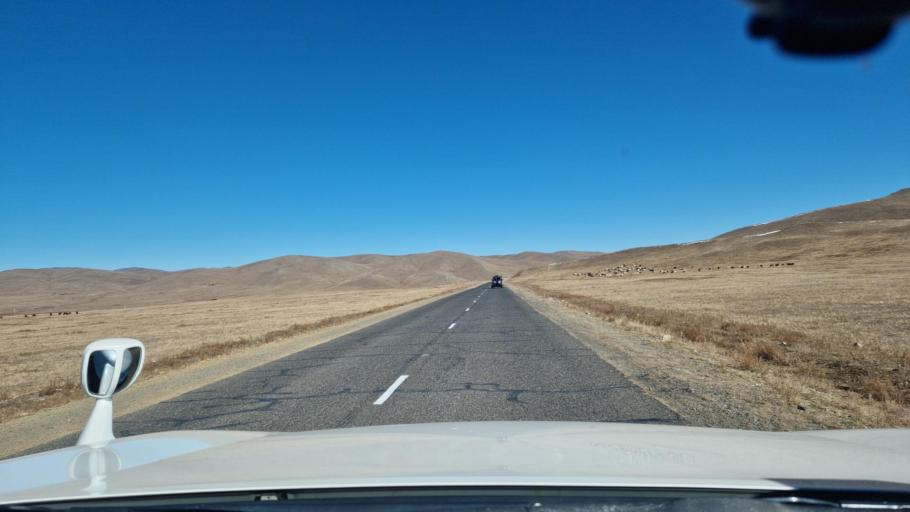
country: MN
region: Hentiy
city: Modot
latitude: 47.8042
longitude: 108.7814
